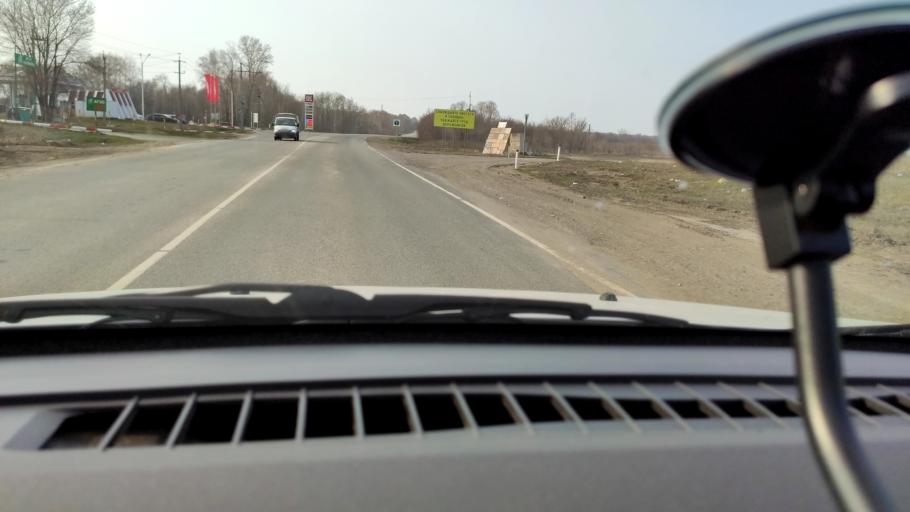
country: RU
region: Samara
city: Dubovyy Umet
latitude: 53.0656
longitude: 50.3701
